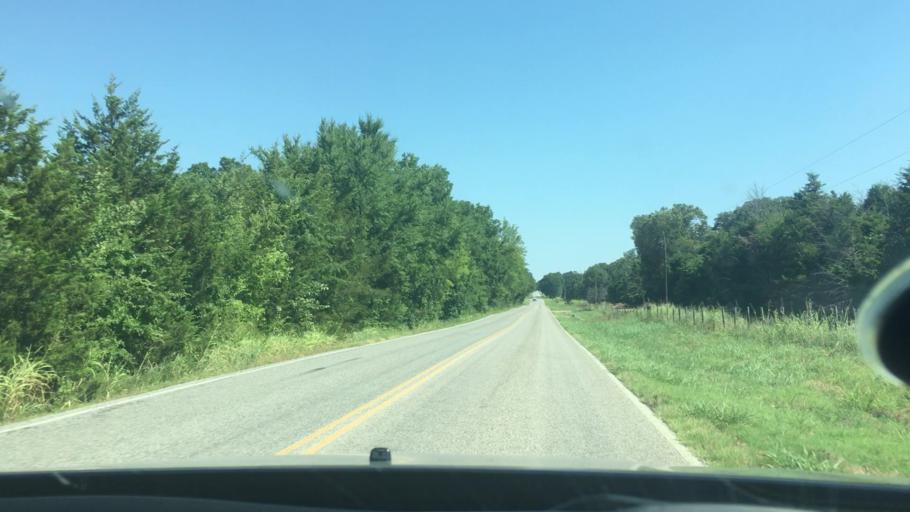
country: US
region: Oklahoma
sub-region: Johnston County
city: Tishomingo
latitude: 34.2832
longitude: -96.6185
